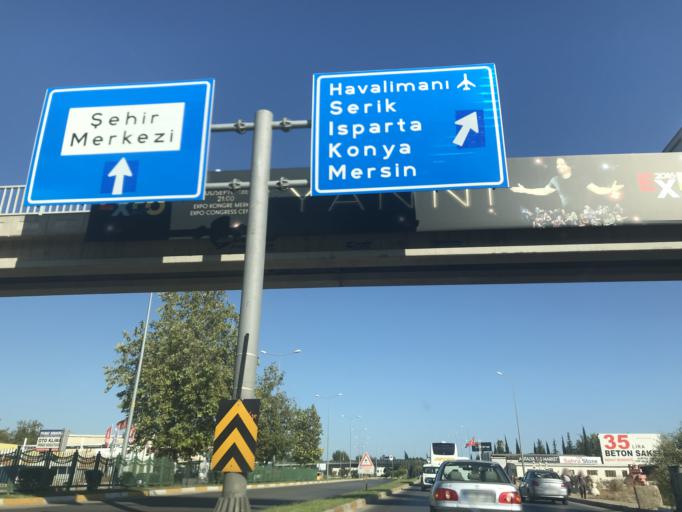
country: TR
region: Antalya
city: Antalya
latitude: 36.9013
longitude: 30.7597
